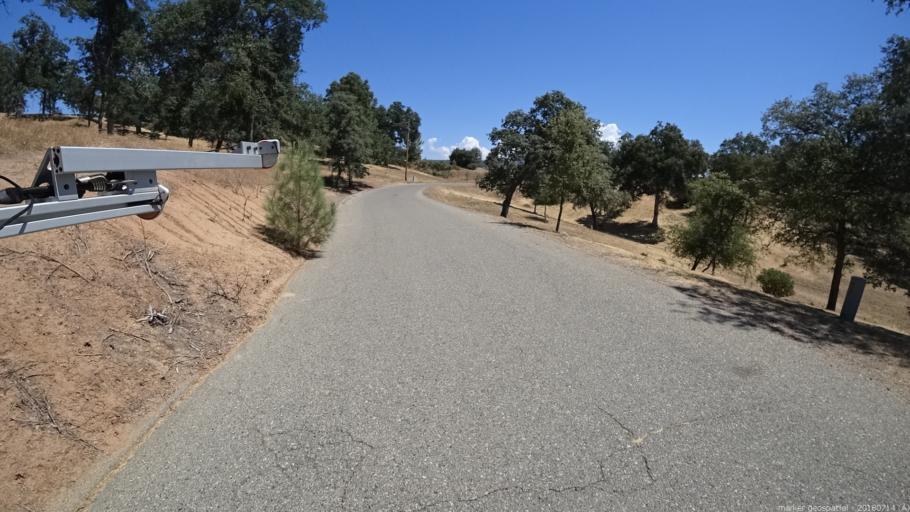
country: US
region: California
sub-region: Madera County
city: Oakhurst
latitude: 37.3626
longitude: -119.6582
